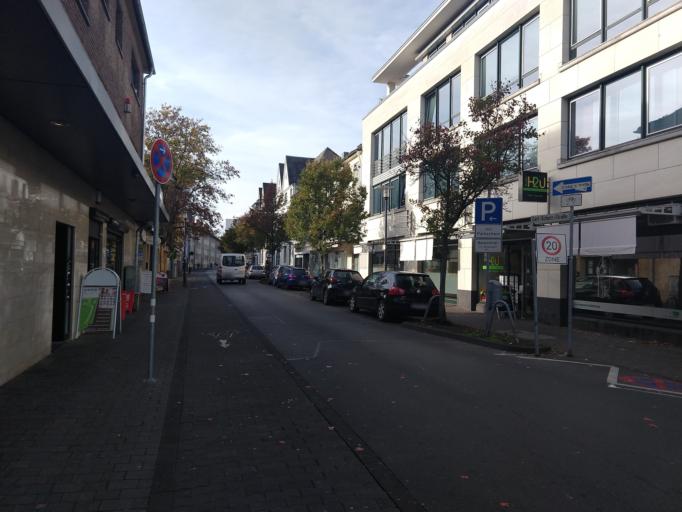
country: DE
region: North Rhine-Westphalia
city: Bruhl
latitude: 50.8283
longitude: 6.9019
